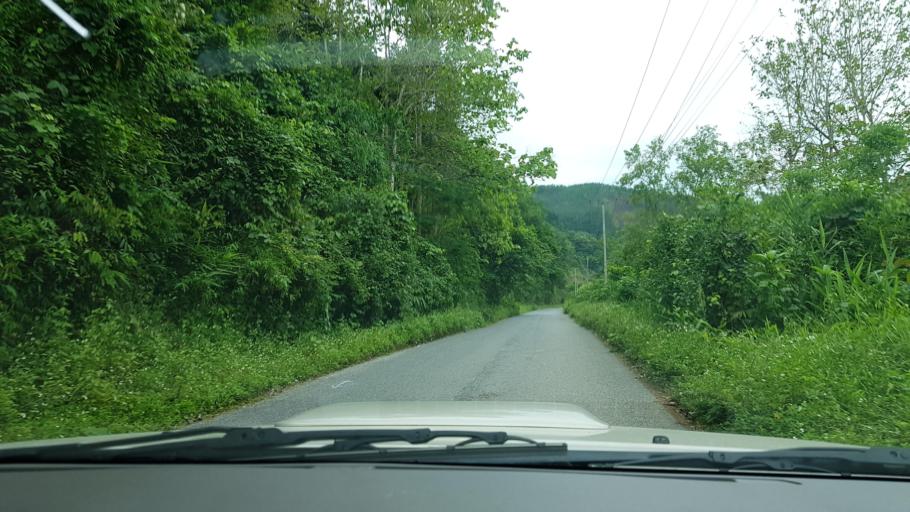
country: LA
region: Phongsali
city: Khoa
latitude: 21.0498
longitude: 102.4098
